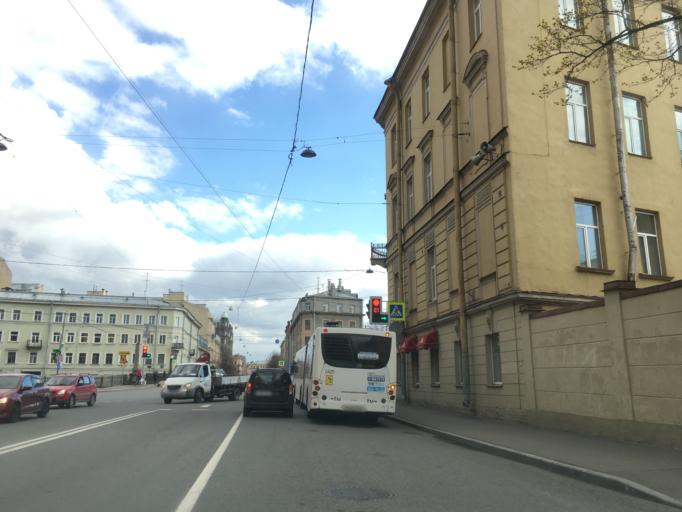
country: RU
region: St.-Petersburg
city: Admiralteisky
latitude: 59.9213
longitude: 30.2866
